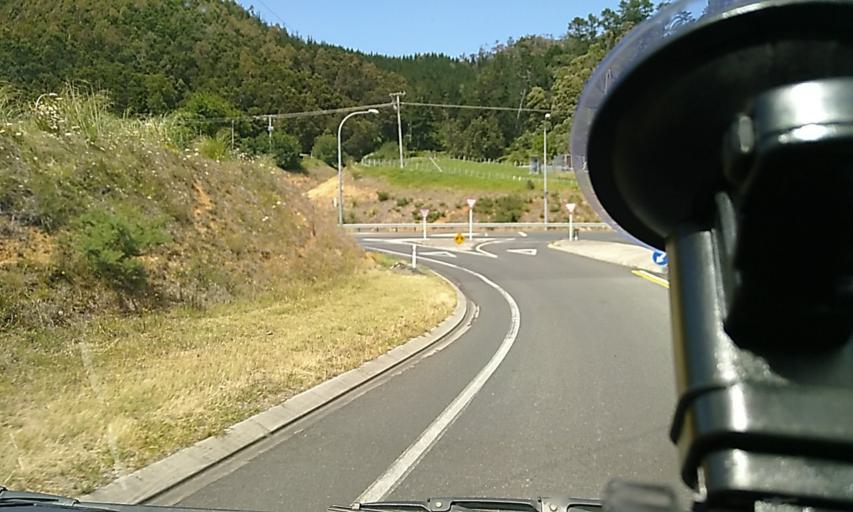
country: NZ
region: Bay of Plenty
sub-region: Western Bay of Plenty District
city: Waihi Beach
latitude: -37.4591
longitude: 175.9305
